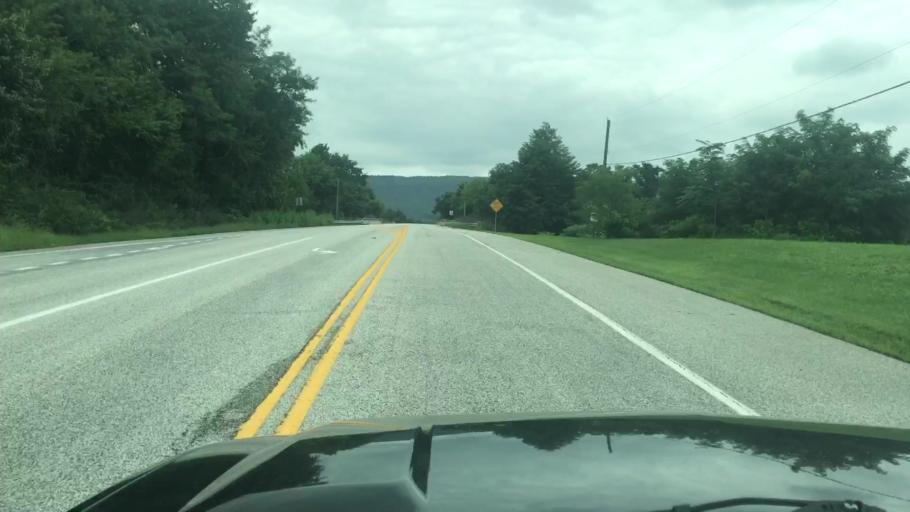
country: US
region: Pennsylvania
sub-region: Cumberland County
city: Enola
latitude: 40.2749
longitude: -76.9865
